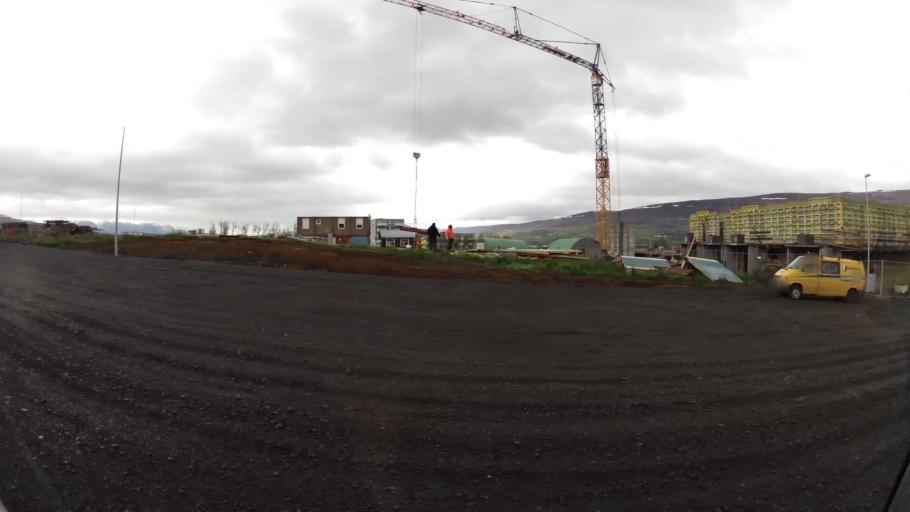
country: IS
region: Northeast
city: Akureyri
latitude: 65.6599
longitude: -18.0983
